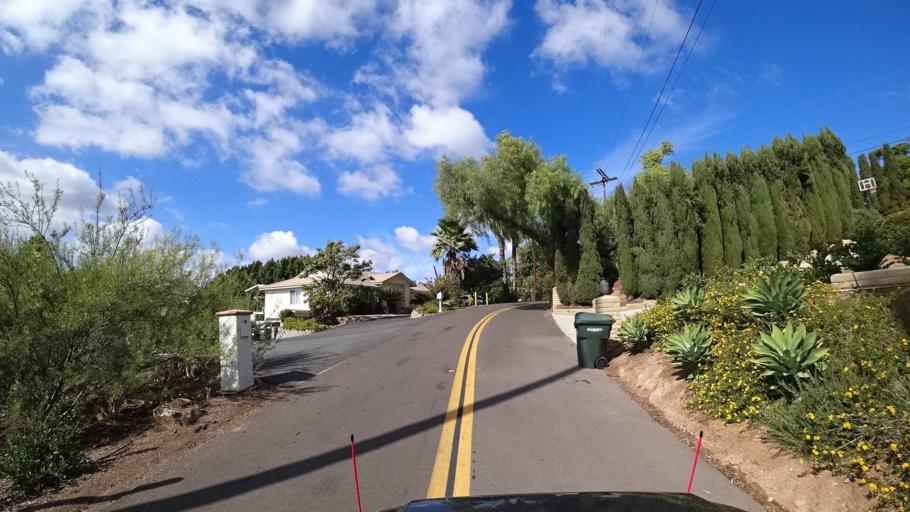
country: US
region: California
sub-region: San Diego County
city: Casa de Oro-Mount Helix
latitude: 32.7590
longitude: -116.9597
